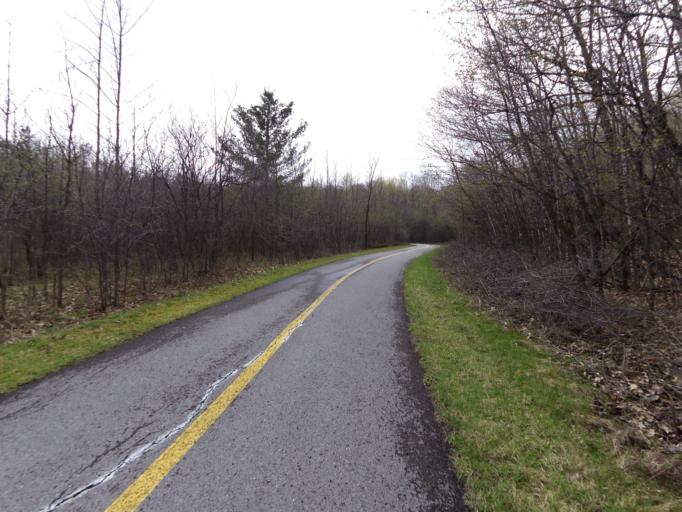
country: CA
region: Quebec
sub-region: Outaouais
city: Gatineau
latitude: 45.4679
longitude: -75.7795
